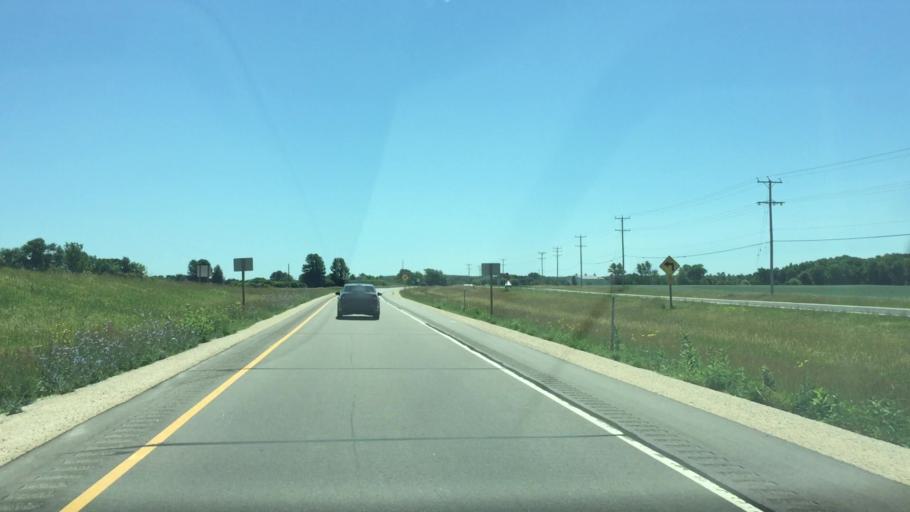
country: US
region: Wisconsin
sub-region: Outagamie County
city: Combined Locks
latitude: 44.2061
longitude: -88.3325
